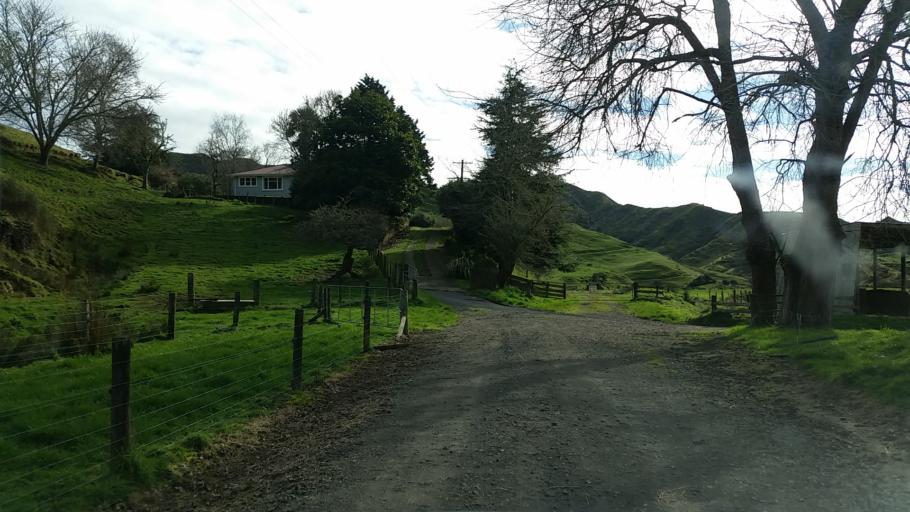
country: NZ
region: Taranaki
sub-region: South Taranaki District
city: Eltham
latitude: -39.2239
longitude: 174.5629
